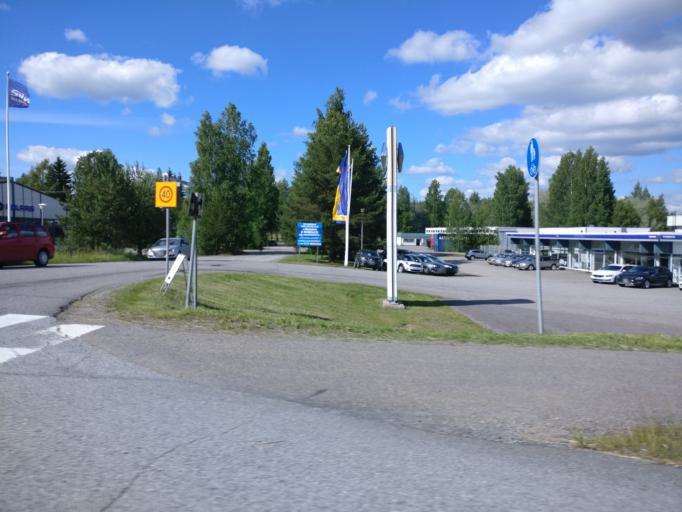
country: FI
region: Southern Savonia
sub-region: Savonlinna
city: Savonlinna
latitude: 61.8775
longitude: 28.9761
